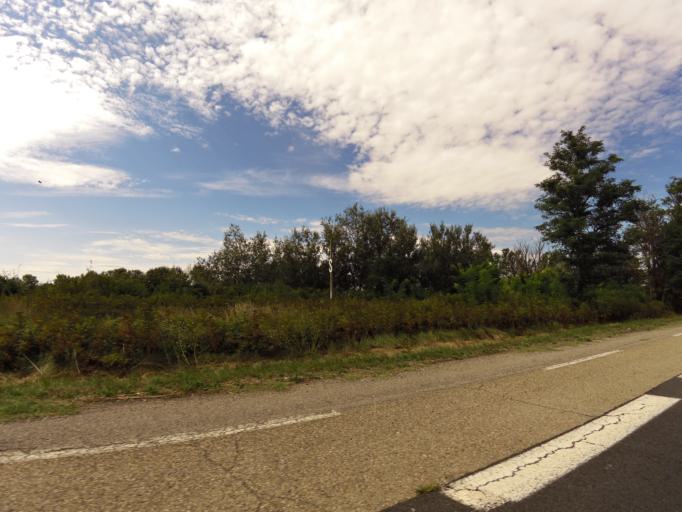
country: FR
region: Languedoc-Roussillon
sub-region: Departement de l'Herault
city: Marsillargues
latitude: 43.6452
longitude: 4.1966
